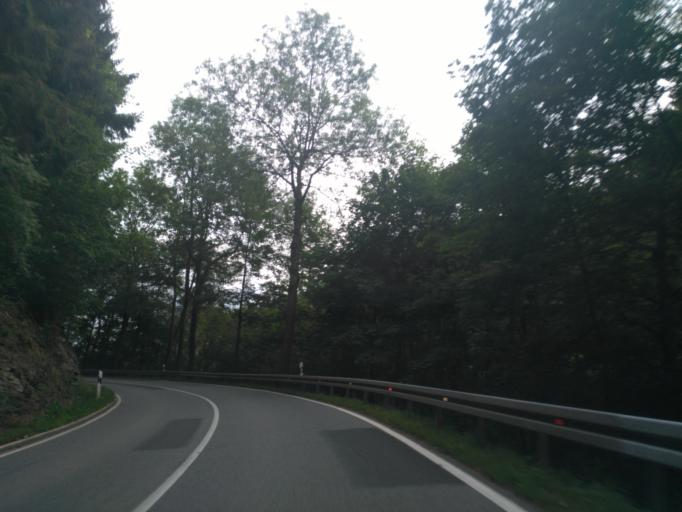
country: DE
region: Saxony
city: Tannenberg
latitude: 50.5975
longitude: 12.9476
